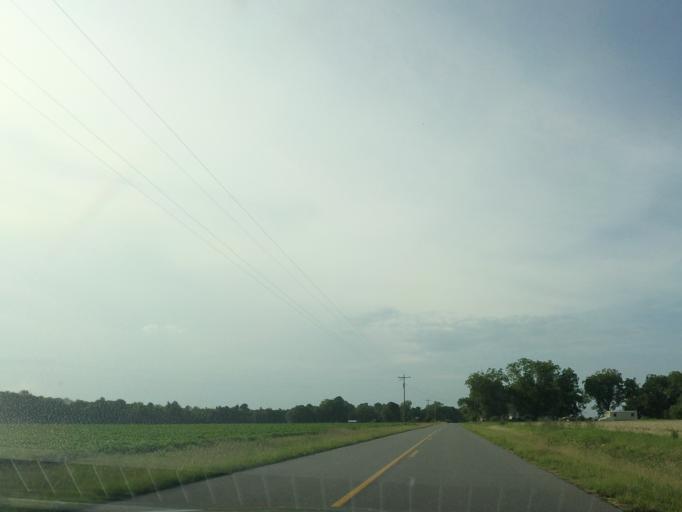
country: US
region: Georgia
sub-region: Bleckley County
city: Cochran
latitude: 32.5173
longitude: -83.3058
